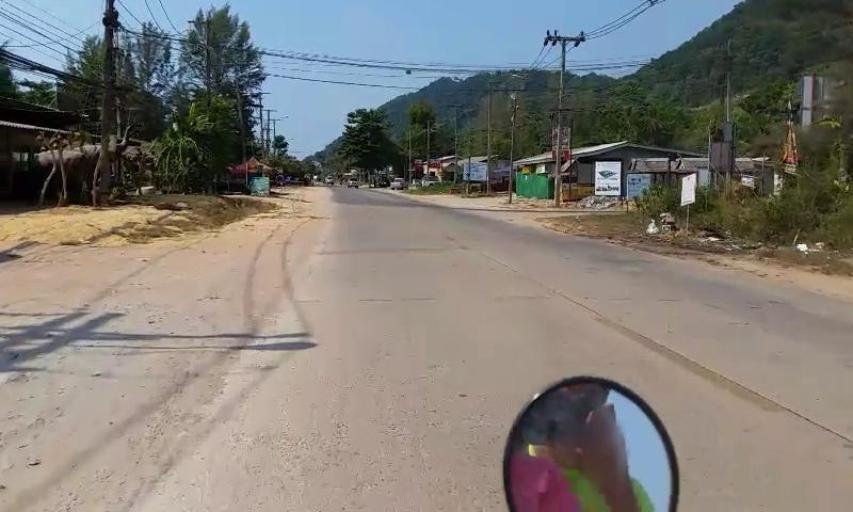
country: TH
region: Krabi
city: Saladan
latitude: 7.6250
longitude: 99.0332
